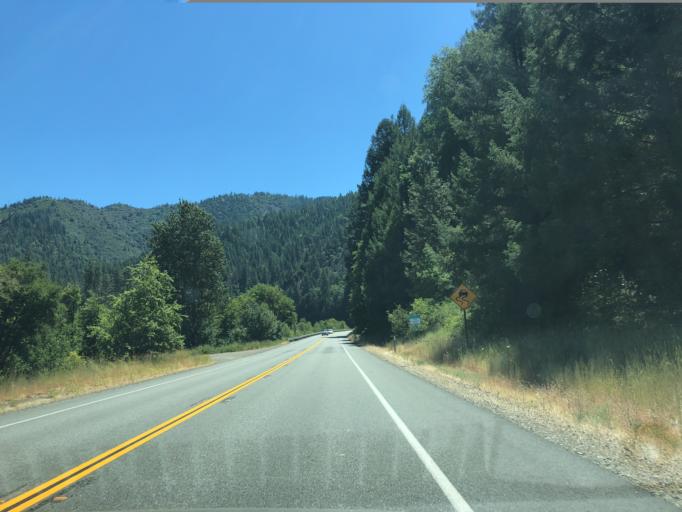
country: US
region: California
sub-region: Trinity County
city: Weaverville
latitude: 40.6538
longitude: -122.9060
